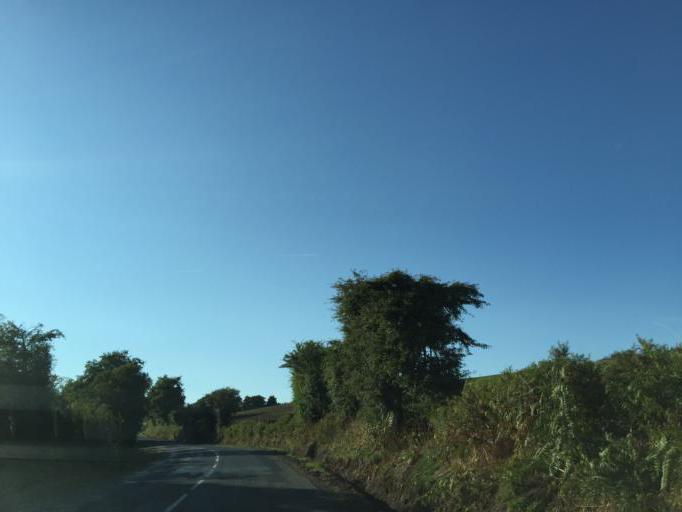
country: FR
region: Midi-Pyrenees
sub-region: Departement de l'Aveyron
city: Salles-Curan
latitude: 44.1303
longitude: 2.8888
